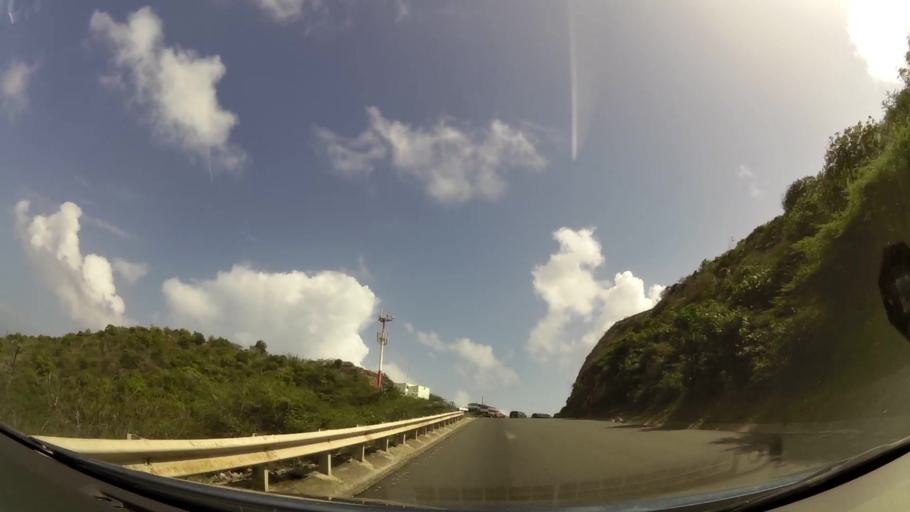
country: KN
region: Saint George Basseterre
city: Basseterre
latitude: 17.2813
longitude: -62.6797
